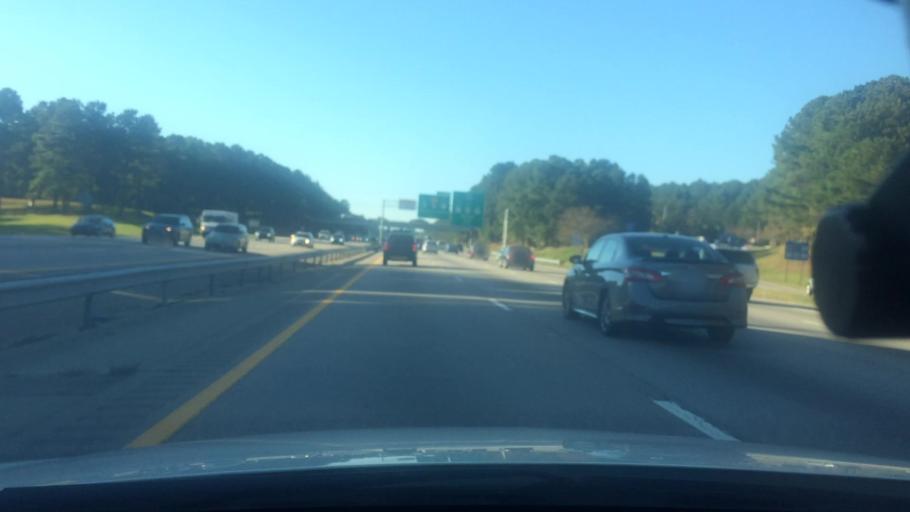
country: US
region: North Carolina
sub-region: Wake County
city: Morrisville
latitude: 35.8597
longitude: -78.8122
